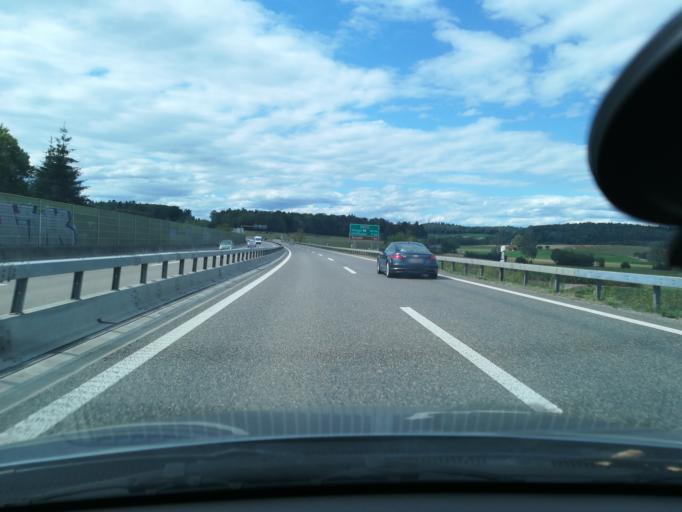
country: CH
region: Zurich
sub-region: Bezirk Andelfingen
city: Kleinandelfingen
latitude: 47.6229
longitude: 8.6813
